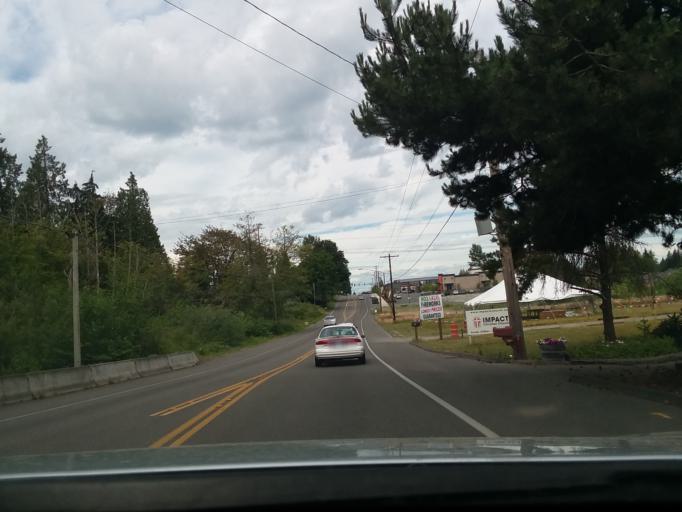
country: US
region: Washington
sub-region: Snohomish County
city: West Lake Stevens
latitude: 47.9782
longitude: -122.1202
